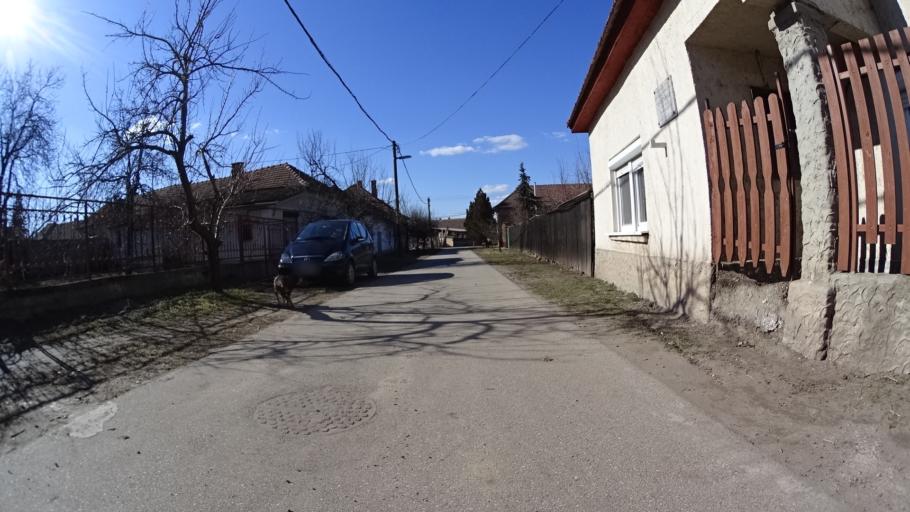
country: HU
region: Bacs-Kiskun
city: Tiszakecske
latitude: 46.9291
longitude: 20.1096
